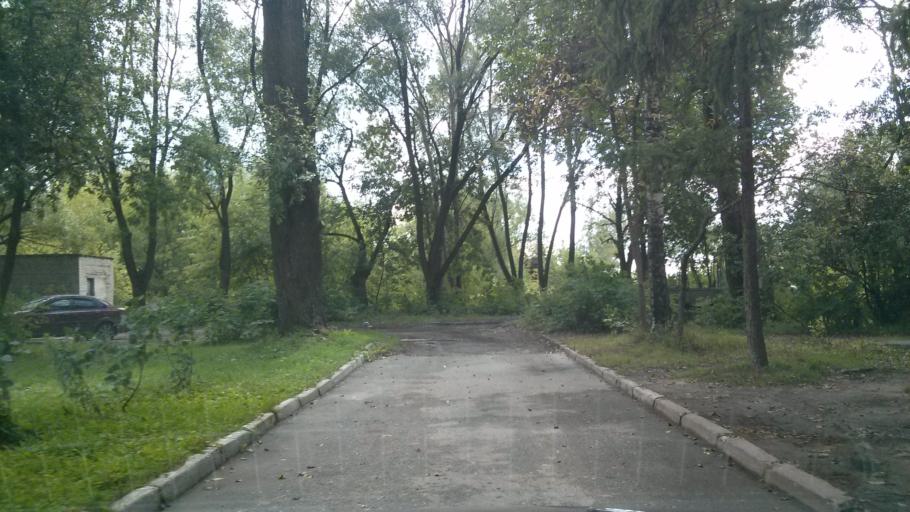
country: RU
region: Vladimir
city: Murom
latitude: 55.5472
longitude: 42.0561
